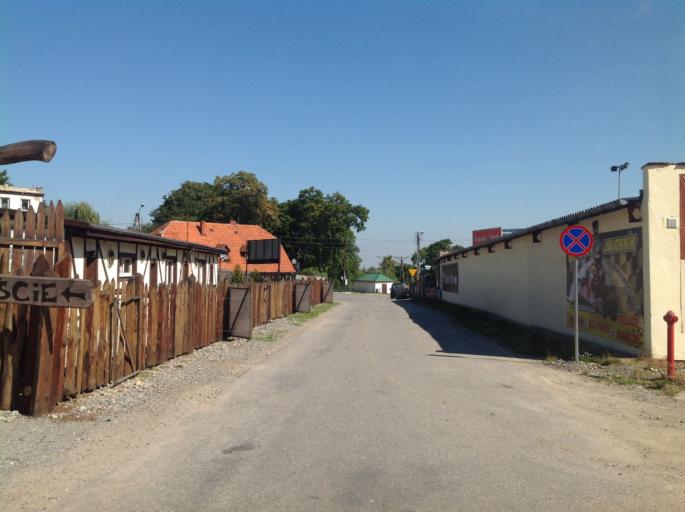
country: PL
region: Lower Silesian Voivodeship
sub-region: Powiat zabkowicki
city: Zloty Stok
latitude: 50.4441
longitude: 16.8791
